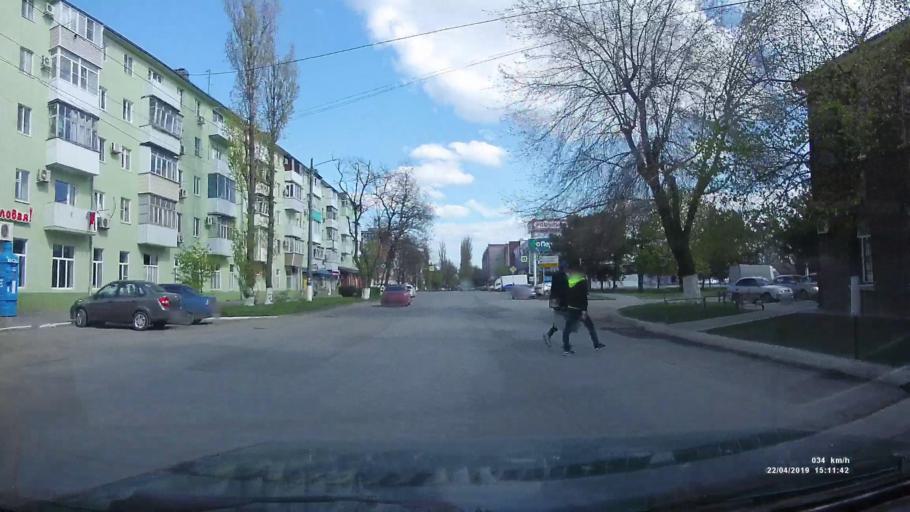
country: RU
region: Rostov
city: Azov
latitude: 47.0999
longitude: 39.4169
